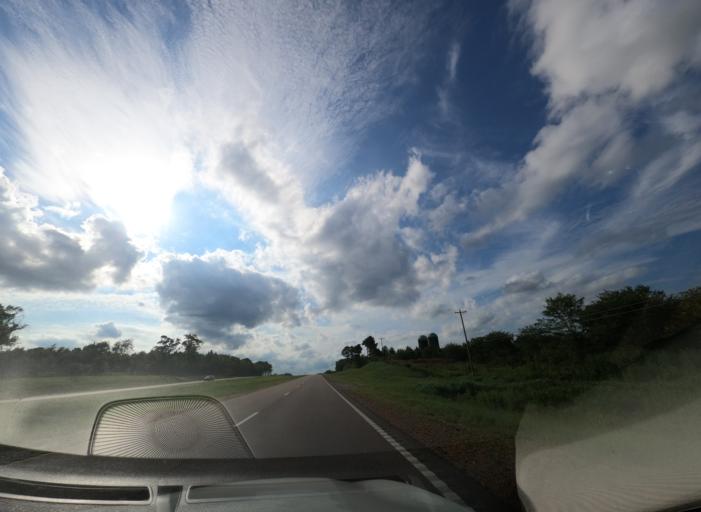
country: US
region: Tennessee
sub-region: Fayette County
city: Piperton
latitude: 34.9762
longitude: -89.5702
